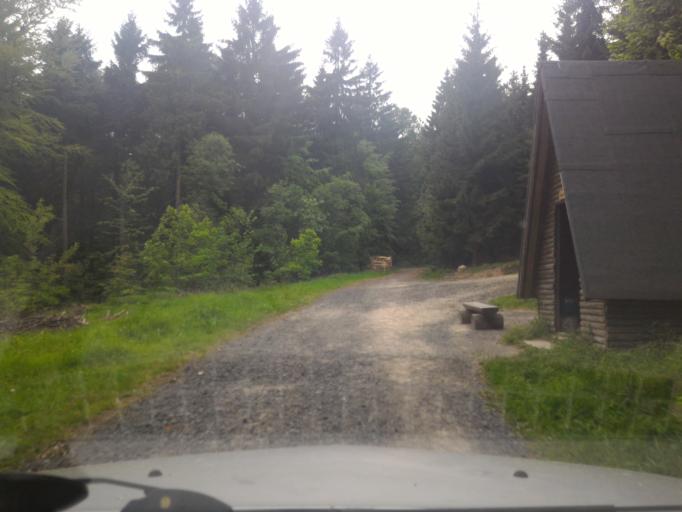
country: DE
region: Saxony
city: Kurort Jonsdorf
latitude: 50.8498
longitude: 14.6750
